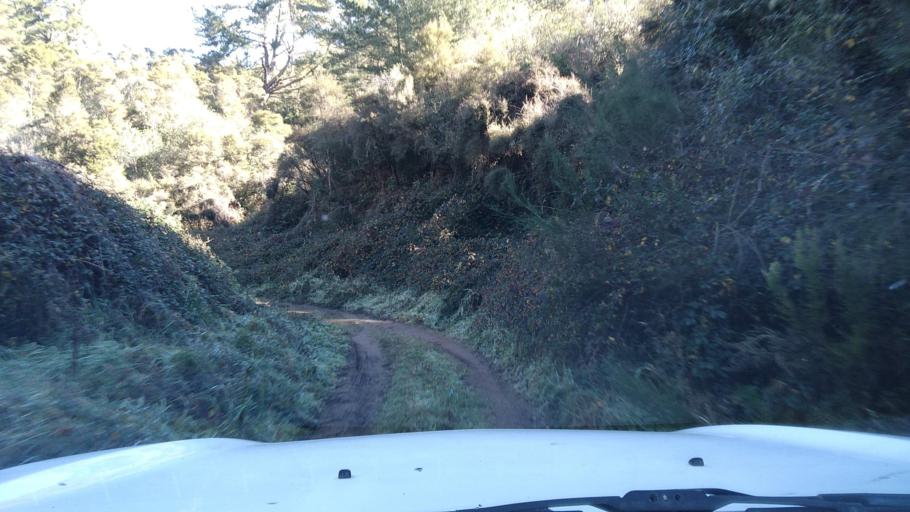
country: NZ
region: Waikato
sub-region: South Waikato District
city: Tokoroa
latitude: -38.3343
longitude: 175.6704
